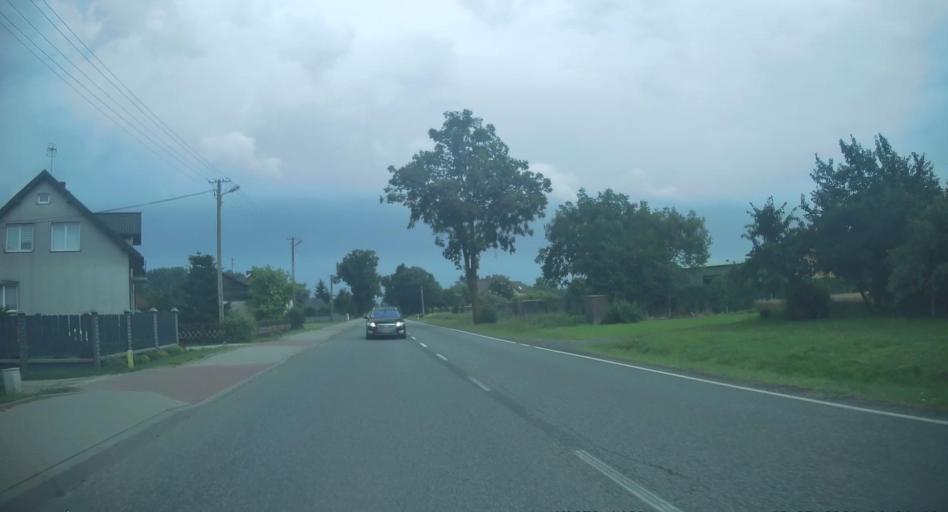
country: PL
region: Lodz Voivodeship
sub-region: Powiat skierniewicki
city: Gluchow
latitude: 51.7753
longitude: 20.1241
